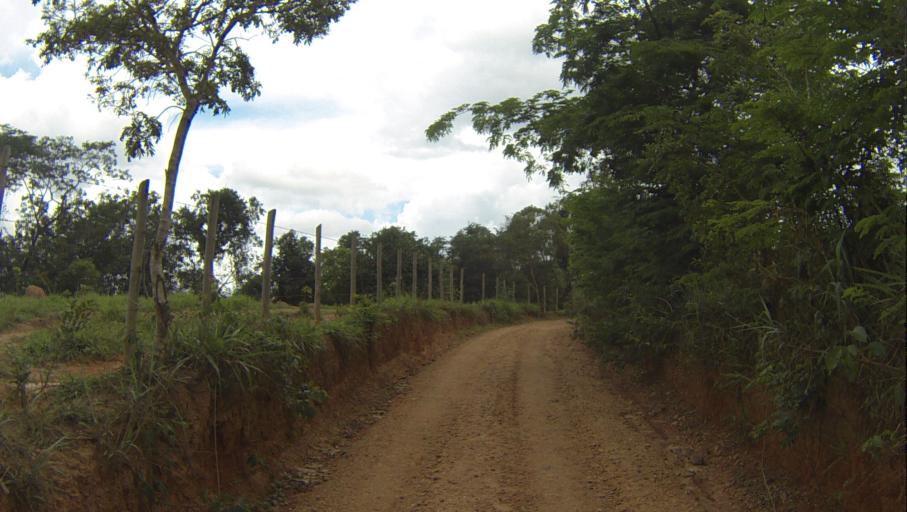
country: BR
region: Minas Gerais
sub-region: Brumadinho
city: Brumadinho
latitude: -20.1665
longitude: -44.1255
